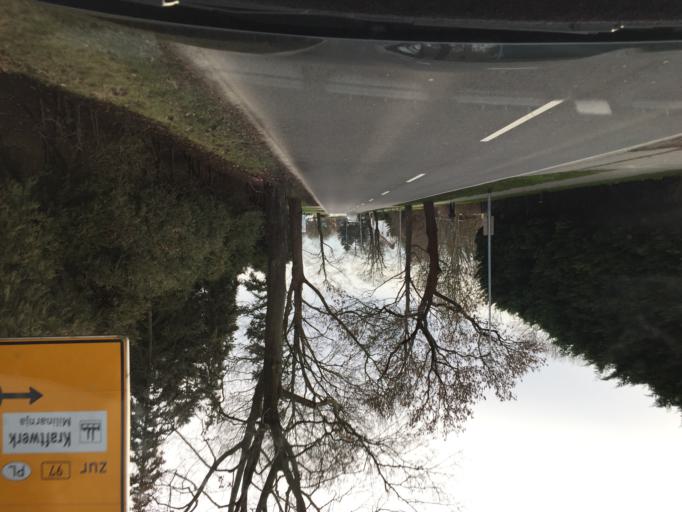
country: DE
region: Brandenburg
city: Peitz
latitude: 51.8547
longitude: 14.4095
